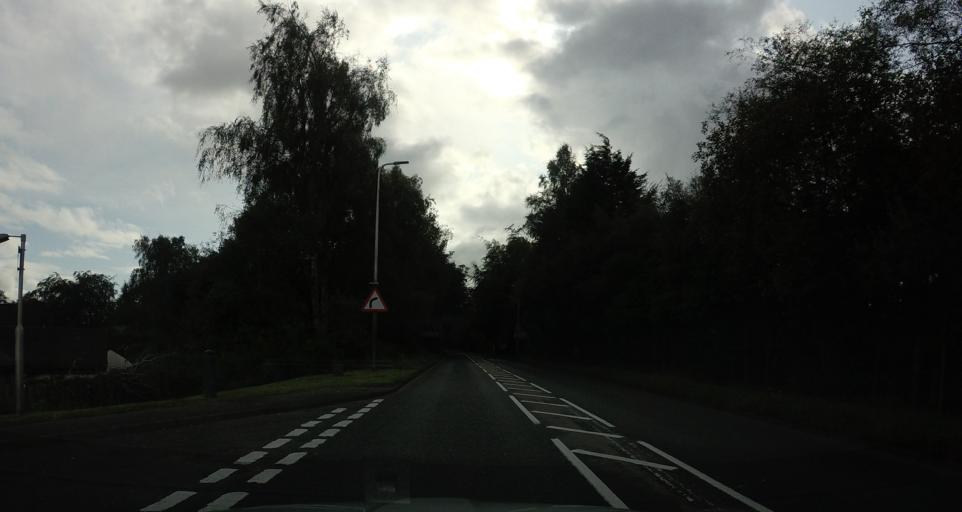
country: GB
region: Scotland
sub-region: Fife
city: Saline
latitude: 56.1823
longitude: -3.5638
